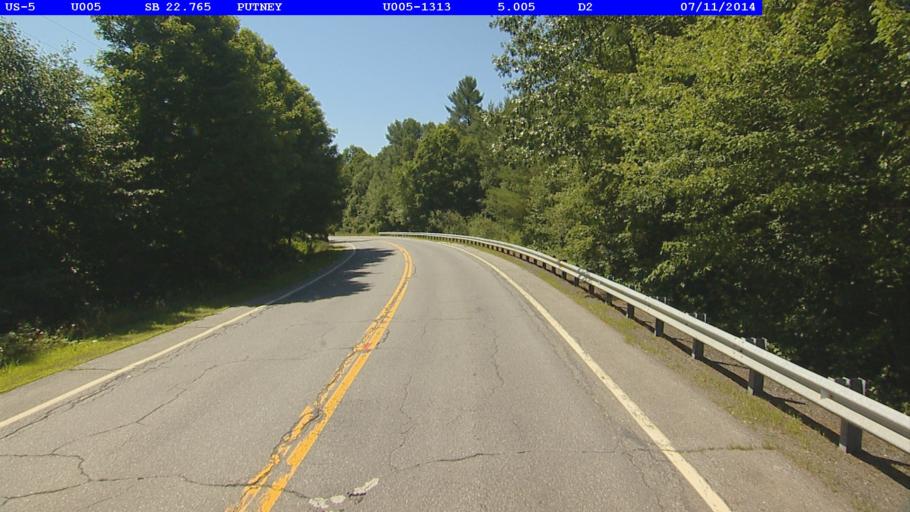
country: US
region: New Hampshire
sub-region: Cheshire County
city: Westmoreland
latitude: 43.0120
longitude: -72.4702
